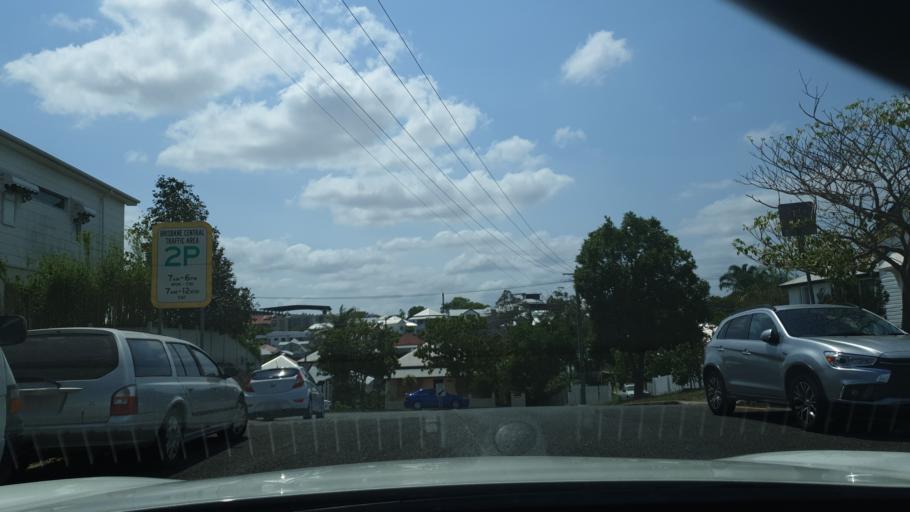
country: AU
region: Queensland
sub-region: Brisbane
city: South Brisbane
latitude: -27.4860
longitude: 153.0212
